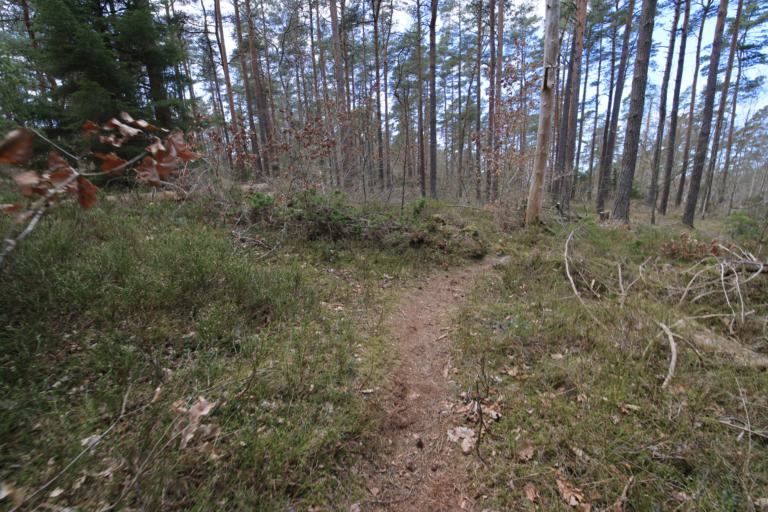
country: SE
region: Halland
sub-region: Varbergs Kommun
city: Varberg
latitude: 57.1819
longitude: 12.2347
